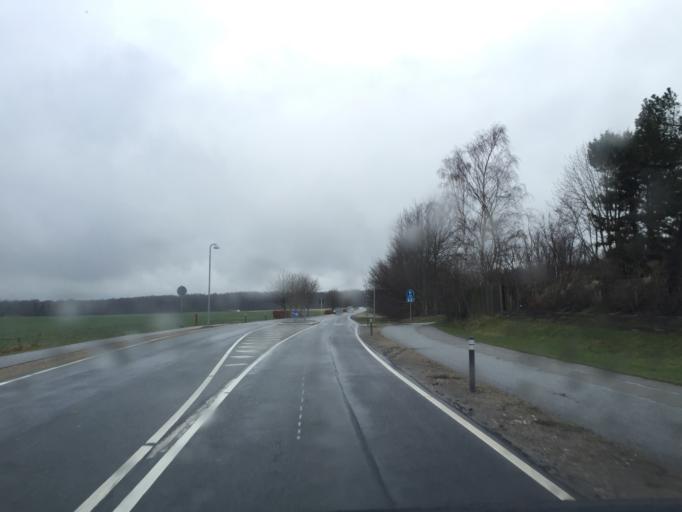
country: DK
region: Capital Region
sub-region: Fureso Kommune
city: Farum
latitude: 55.8142
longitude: 12.3446
